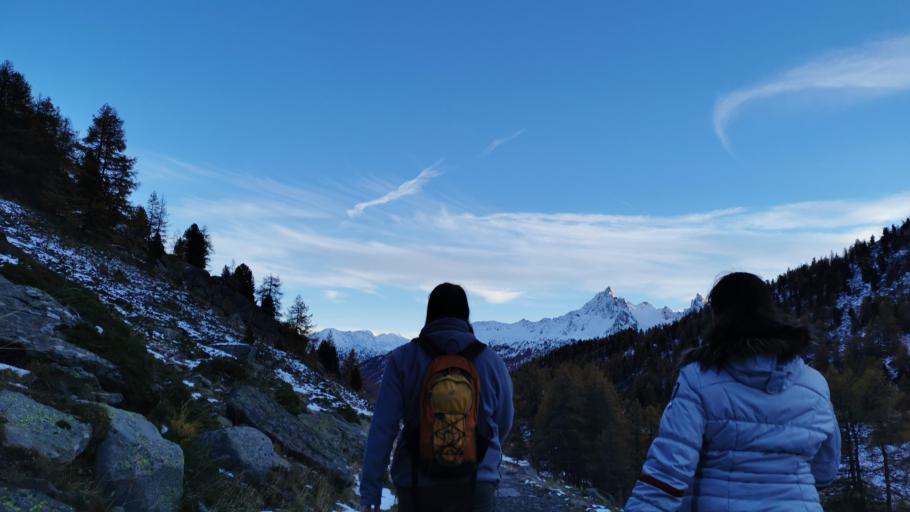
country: FR
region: Provence-Alpes-Cote d'Azur
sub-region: Departement des Hautes-Alpes
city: Le Monetier-les-Bains
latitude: 45.0632
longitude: 6.5225
